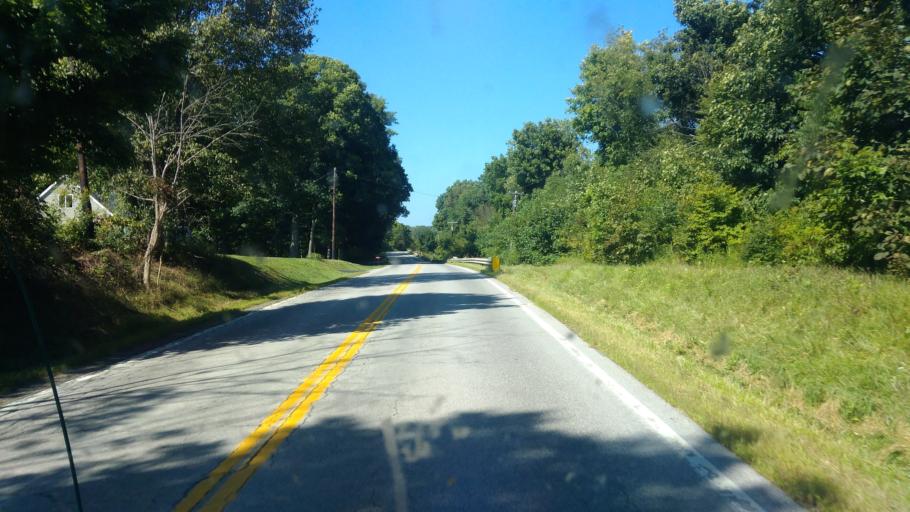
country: US
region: Ohio
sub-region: Ashland County
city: Ashland
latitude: 40.9420
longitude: -82.2663
